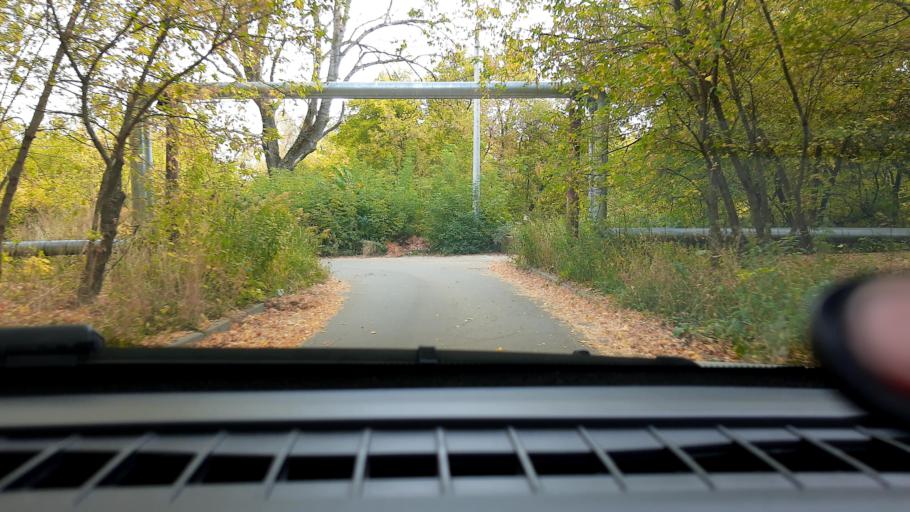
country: RU
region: Nizjnij Novgorod
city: Nizhniy Novgorod
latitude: 56.2434
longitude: 43.9578
